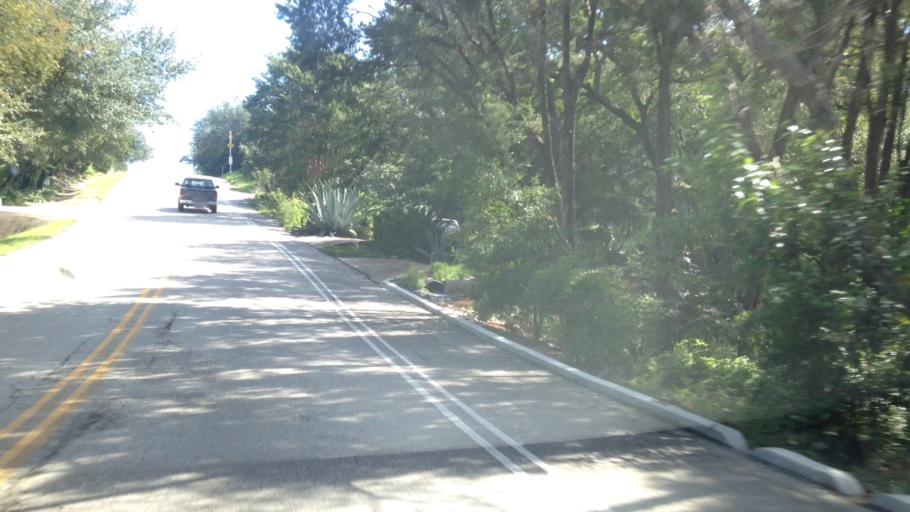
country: US
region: Texas
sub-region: Travis County
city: Lakeway
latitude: 30.3594
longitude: -97.9695
